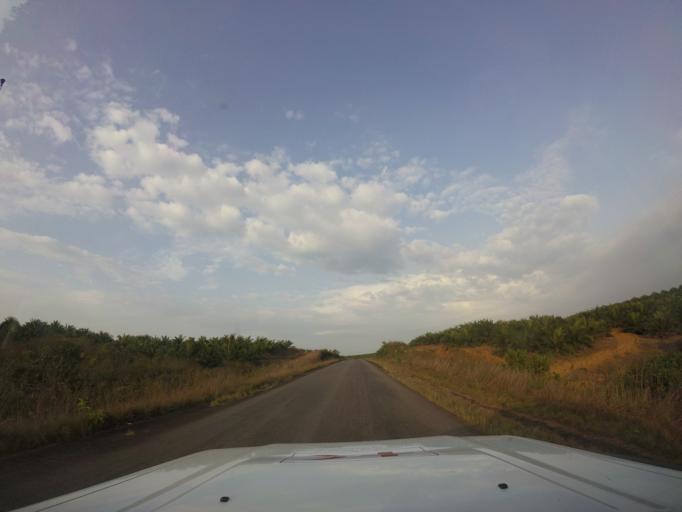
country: LR
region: Bomi
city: Tubmanburg
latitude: 6.7246
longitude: -11.0487
